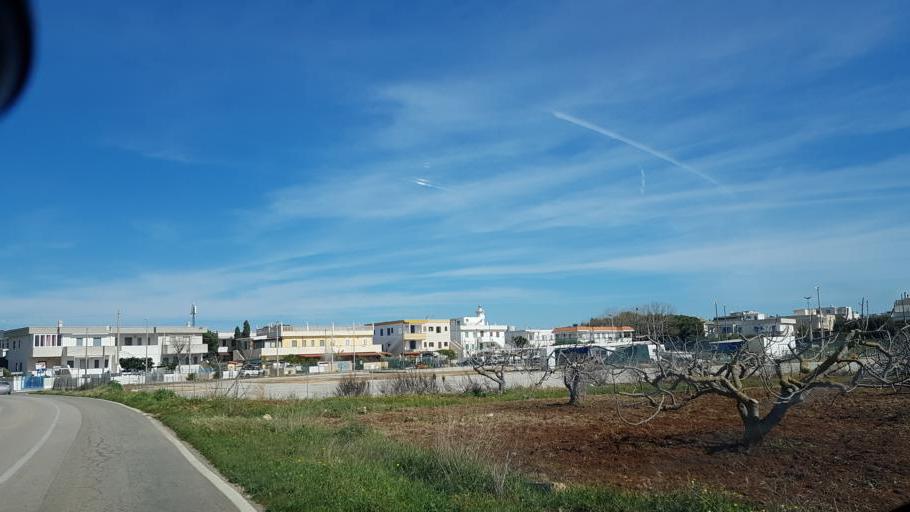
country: IT
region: Apulia
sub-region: Provincia di Brindisi
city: Pezze di Greco
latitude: 40.8402
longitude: 17.4640
